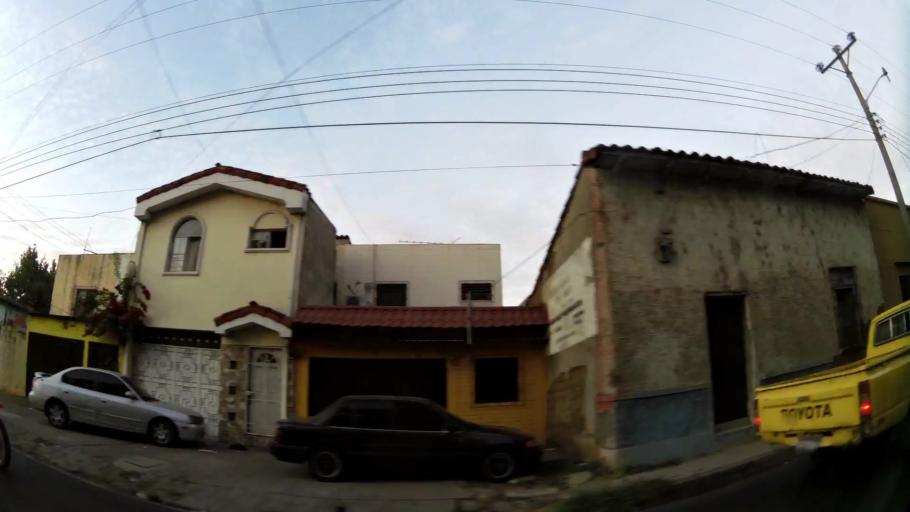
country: SV
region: Santa Ana
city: Santa Ana
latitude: 13.9893
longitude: -89.5565
